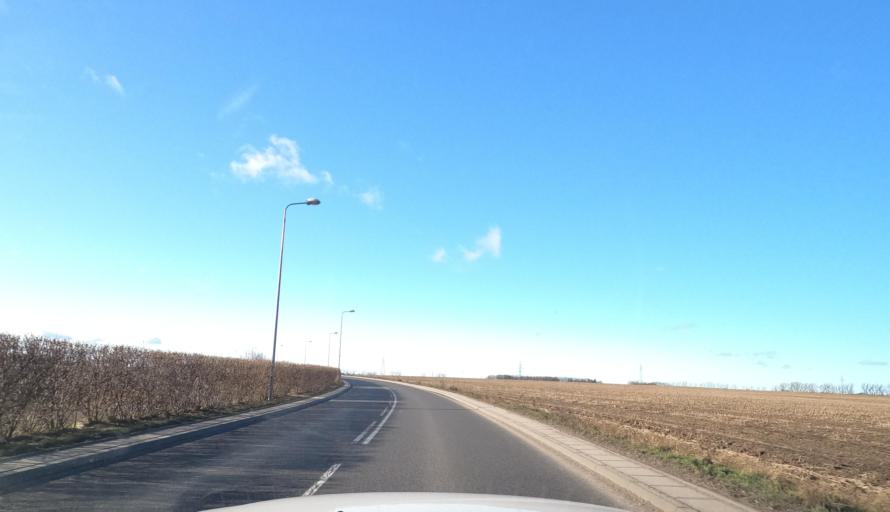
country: PL
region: West Pomeranian Voivodeship
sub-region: Powiat stargardzki
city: Stargard Szczecinski
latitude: 53.3057
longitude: 15.0128
